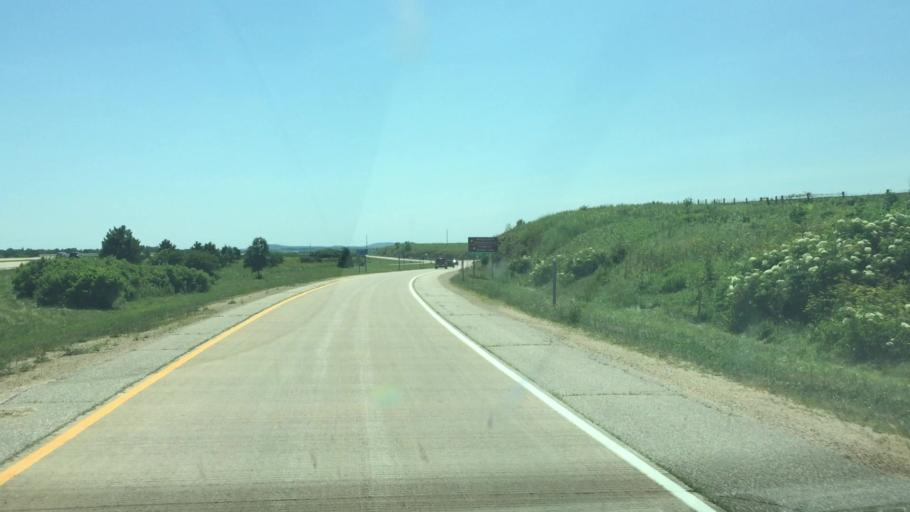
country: US
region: Wisconsin
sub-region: Iowa County
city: Mineral Point
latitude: 42.8884
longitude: -90.1632
